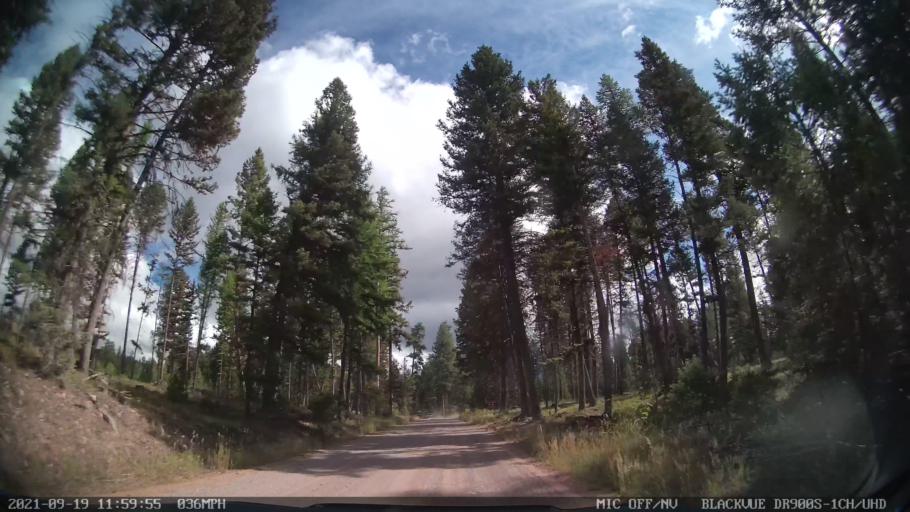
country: US
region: Montana
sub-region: Missoula County
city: Seeley Lake
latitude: 47.1865
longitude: -113.4721
